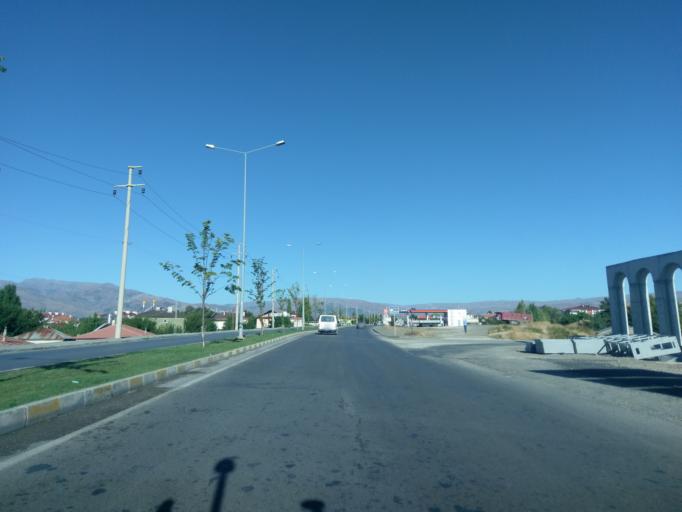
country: TR
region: Erzincan
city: Erzincan
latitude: 39.7501
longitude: 39.4598
